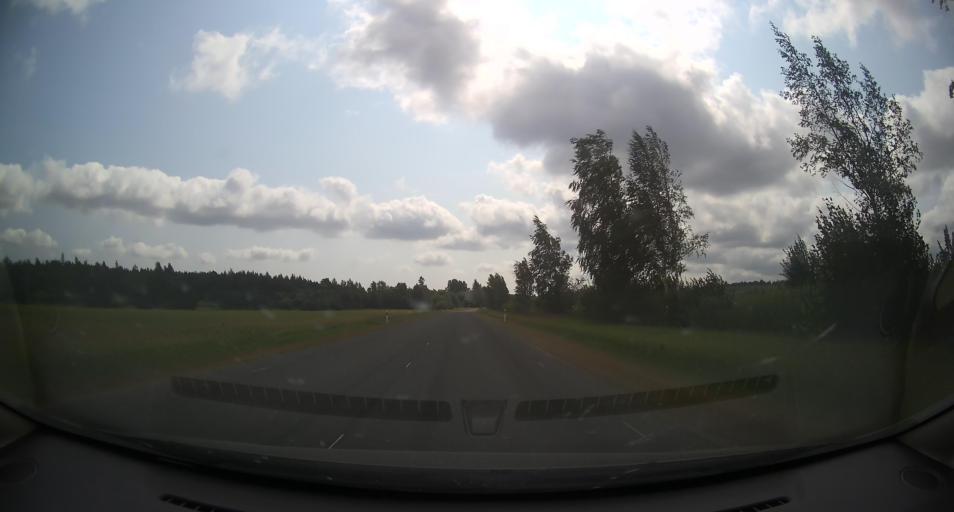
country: EE
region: Paernumaa
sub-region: Audru vald
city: Audru
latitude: 58.4600
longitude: 24.3153
